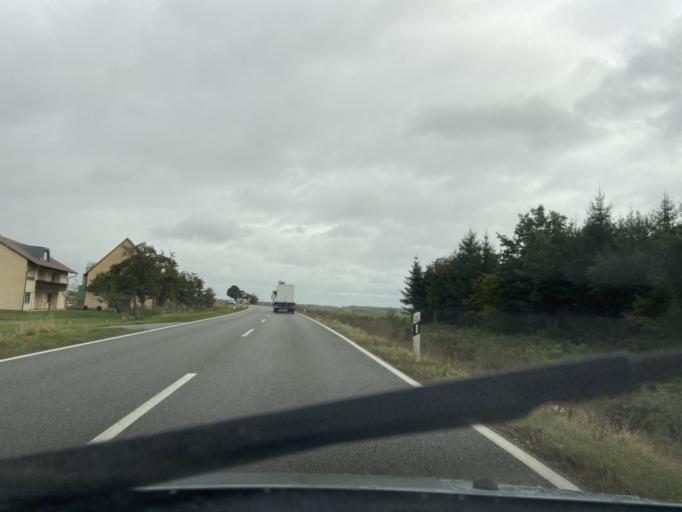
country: DE
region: Baden-Wuerttemberg
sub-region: Tuebingen Region
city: Krauchenwies
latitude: 48.0229
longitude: 9.2697
